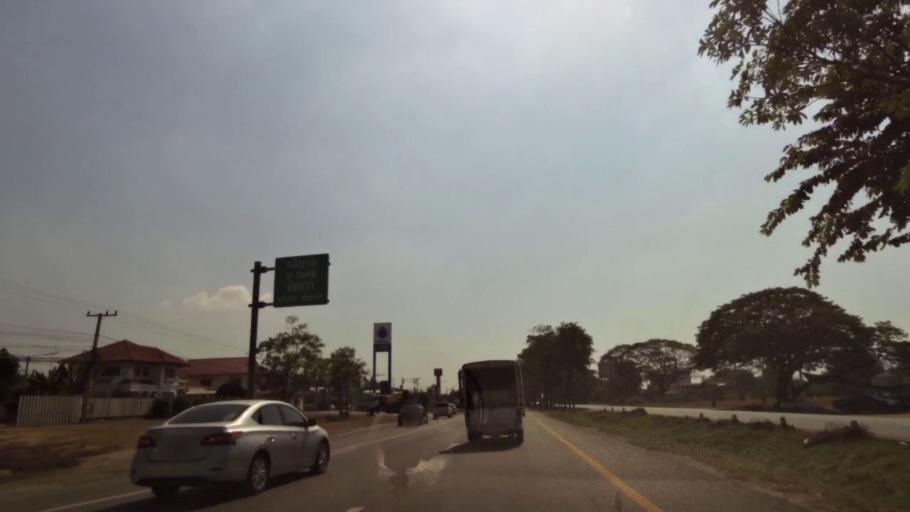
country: TH
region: Phichit
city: Bueng Na Rang
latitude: 16.1196
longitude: 100.1257
